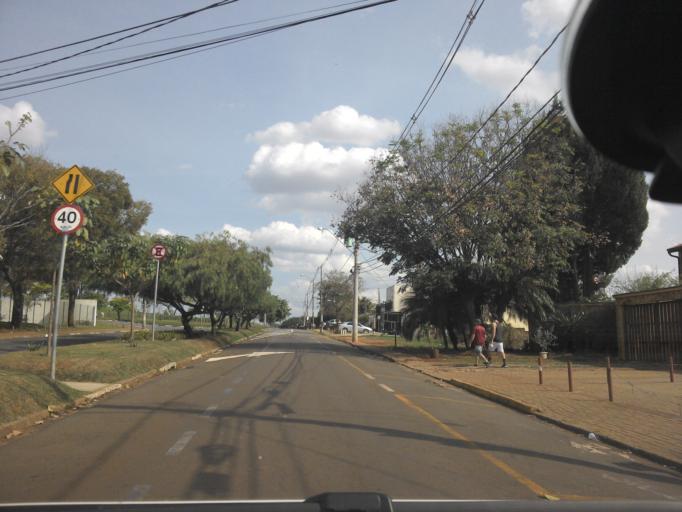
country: BR
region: Sao Paulo
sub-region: Campinas
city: Campinas
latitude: -22.8337
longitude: -47.0534
